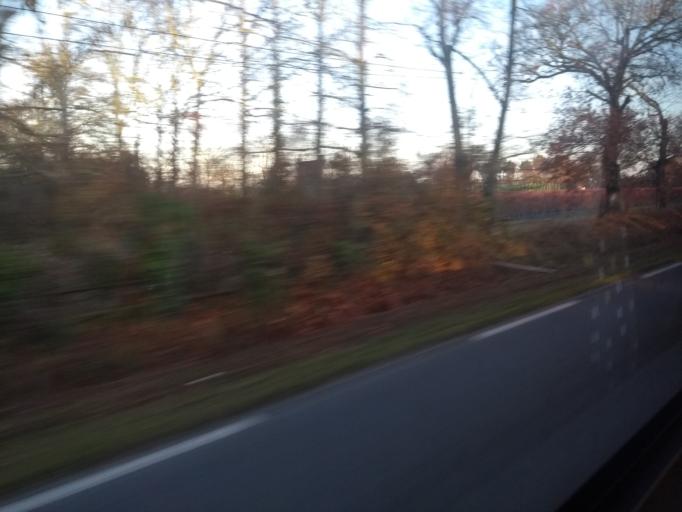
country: FR
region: Aquitaine
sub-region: Departement de la Gironde
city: Le Barp
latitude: 44.6707
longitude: -0.7311
